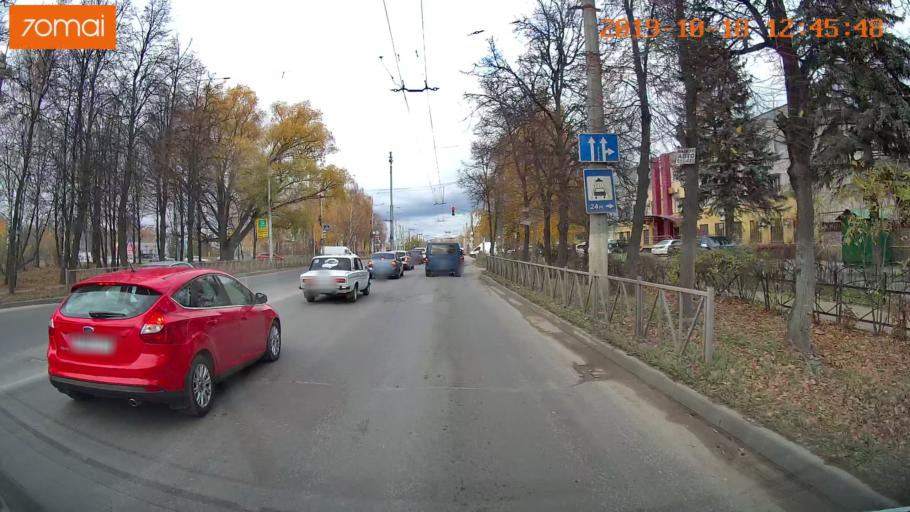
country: RU
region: Rjazan
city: Ryazan'
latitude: 54.6543
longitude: 39.6652
